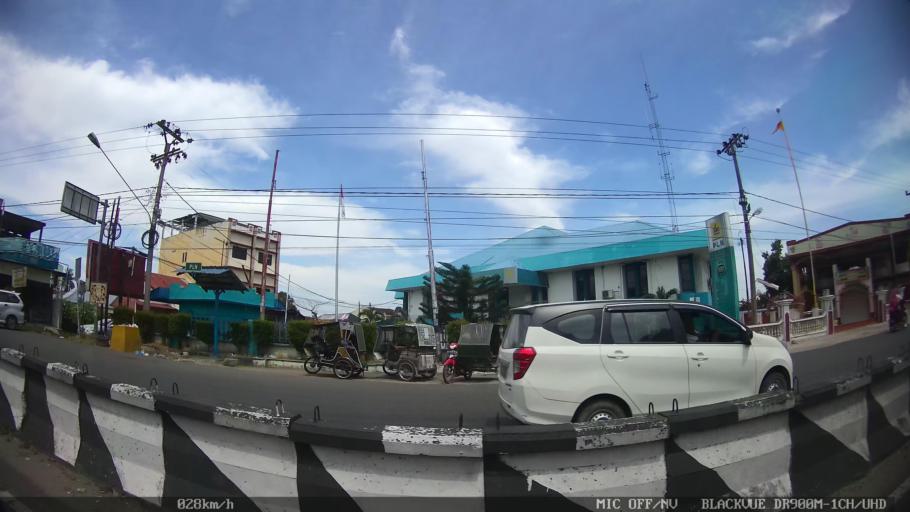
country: ID
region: North Sumatra
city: Binjai
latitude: 3.6144
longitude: 98.4961
